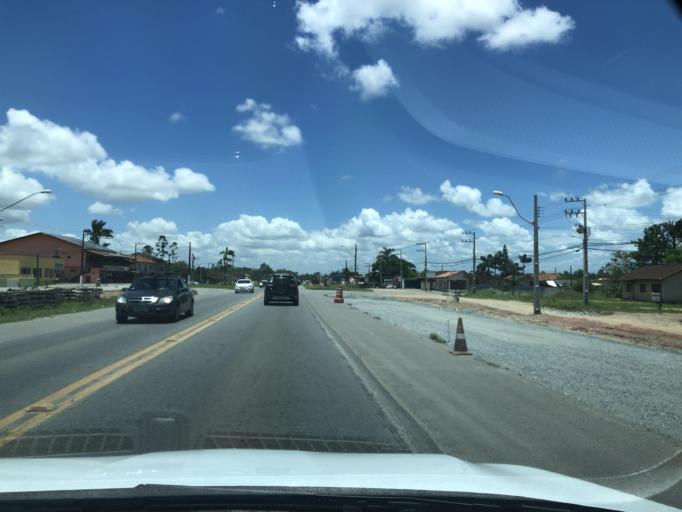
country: BR
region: Santa Catarina
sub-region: Joinville
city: Joinville
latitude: -26.3986
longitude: -48.7414
